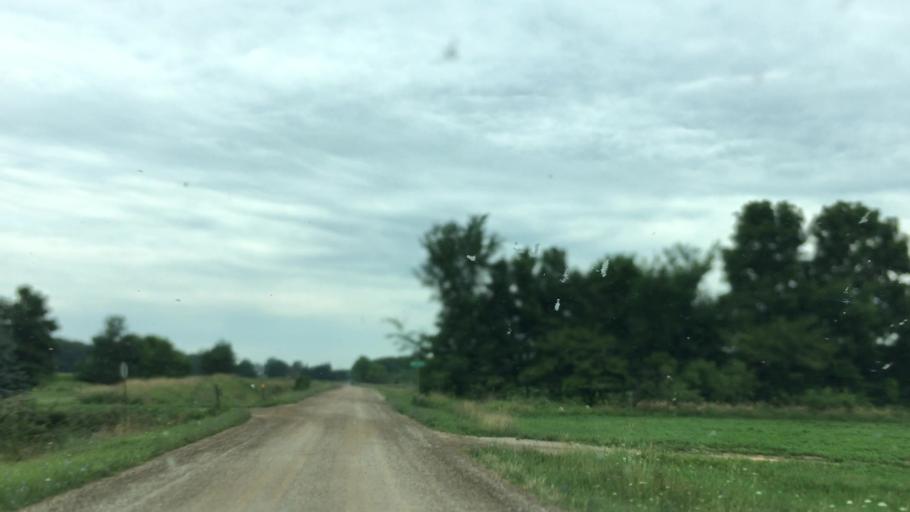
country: US
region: Michigan
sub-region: Clinton County
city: Saint Johns
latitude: 43.0813
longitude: -84.4839
